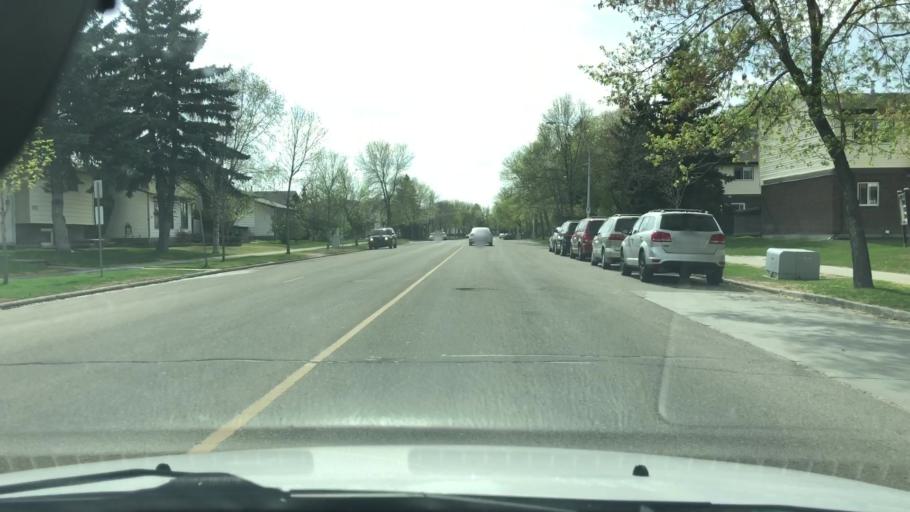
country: CA
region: Alberta
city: Edmonton
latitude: 53.6016
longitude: -113.5222
